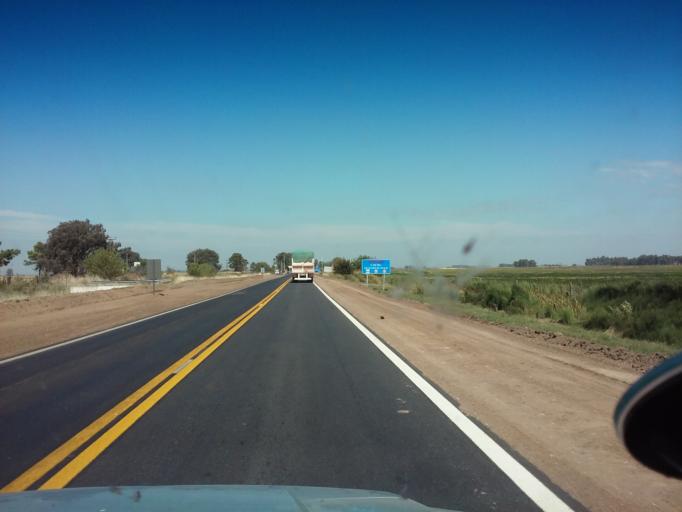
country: AR
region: Buenos Aires
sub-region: Partido de Nueve de Julio
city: Nueve de Julio
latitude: -35.3566
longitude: -60.6984
